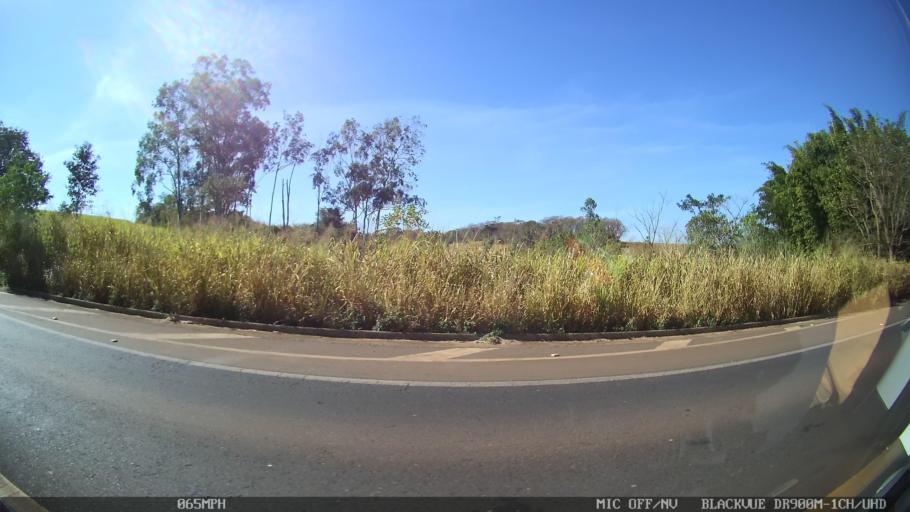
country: BR
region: Sao Paulo
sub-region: Olimpia
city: Olimpia
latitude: -20.6949
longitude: -48.8948
